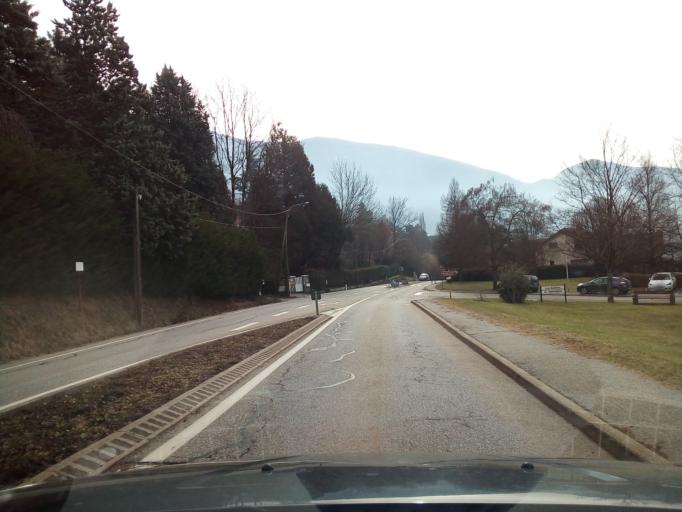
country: FR
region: Rhone-Alpes
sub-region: Departement de l'Isere
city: Vaulnaveys-le-Haut
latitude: 45.1490
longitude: 5.8372
